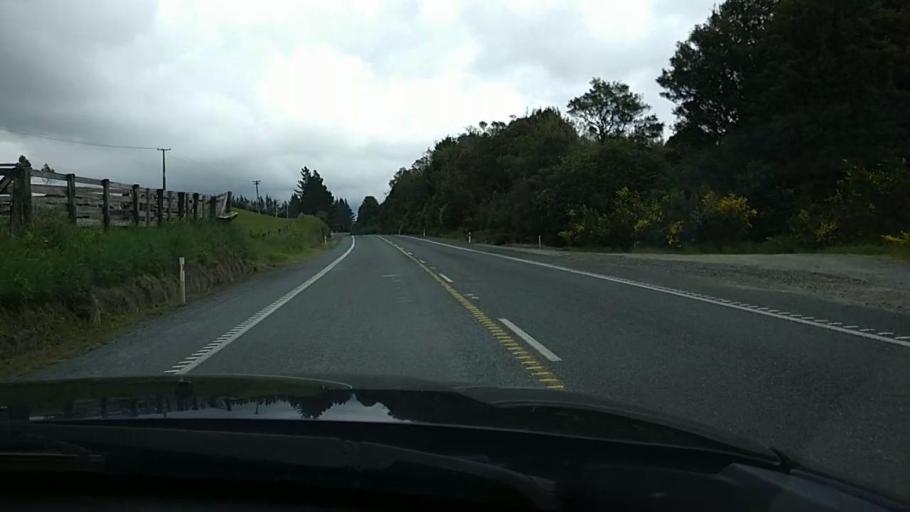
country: NZ
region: Bay of Plenty
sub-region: Rotorua District
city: Rotorua
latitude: -38.0671
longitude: 176.1074
